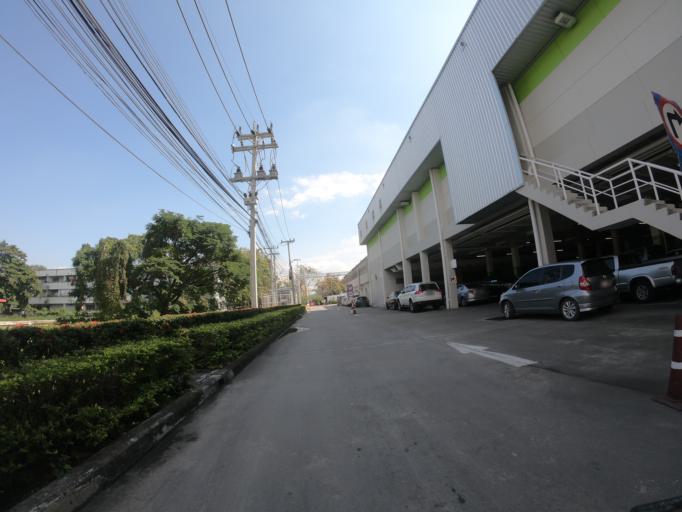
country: TH
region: Chiang Mai
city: Chiang Mai
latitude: 18.7439
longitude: 98.9625
